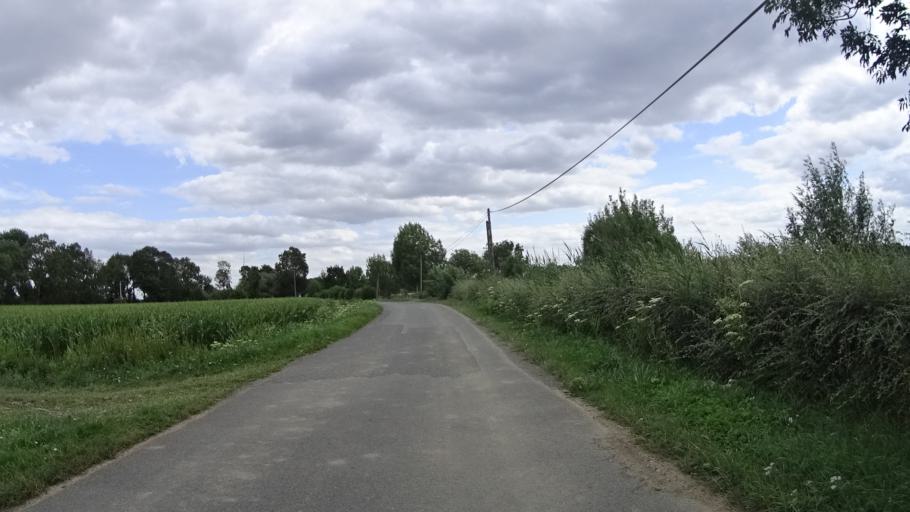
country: FR
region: Pays de la Loire
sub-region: Departement de Maine-et-Loire
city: Saint-Clement-des-Levees
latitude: 47.3564
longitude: -0.1756
